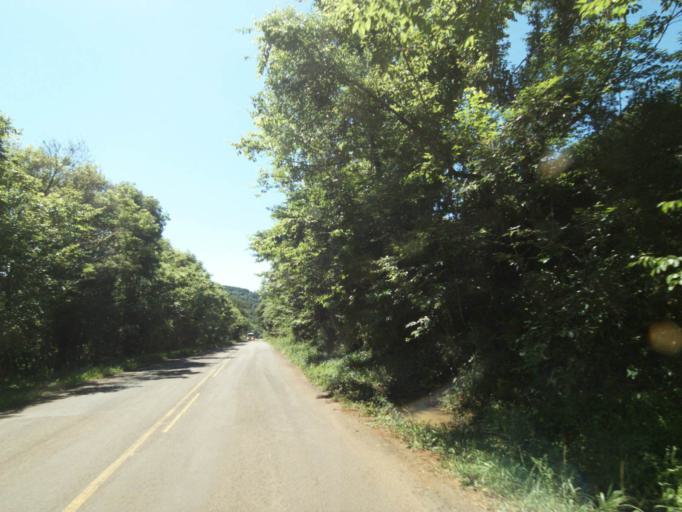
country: BR
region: Parana
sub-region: Ampere
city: Ampere
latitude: -26.1847
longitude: -53.3622
